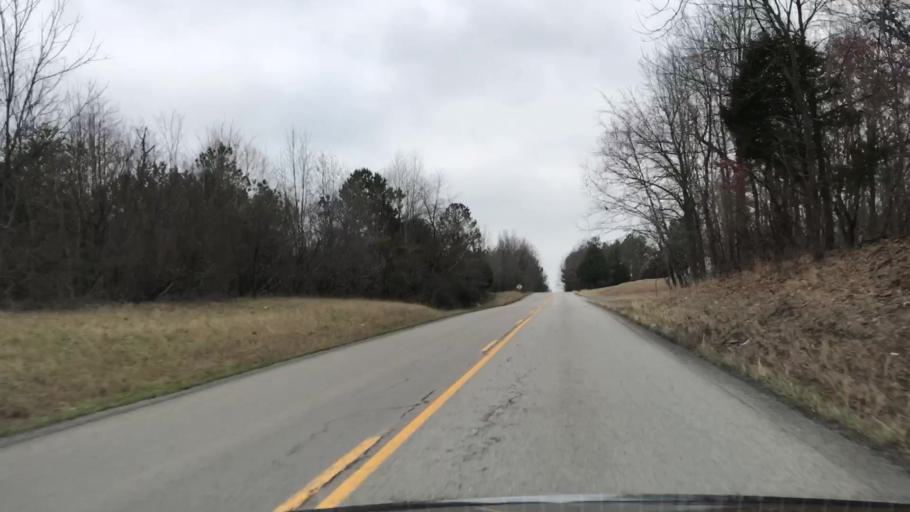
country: US
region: Kentucky
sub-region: Muhlenberg County
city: Morehead
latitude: 37.2803
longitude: -87.2090
